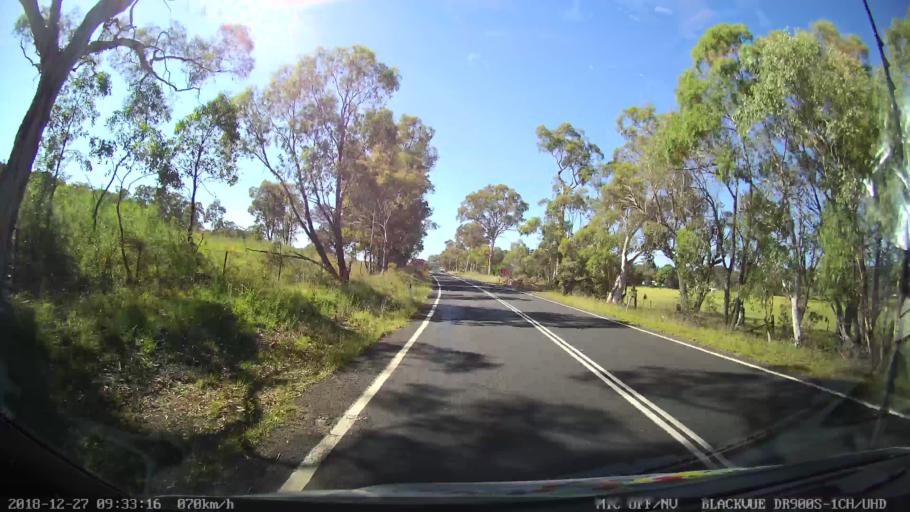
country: AU
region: New South Wales
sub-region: Lithgow
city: Portland
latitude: -33.2170
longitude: 150.0207
